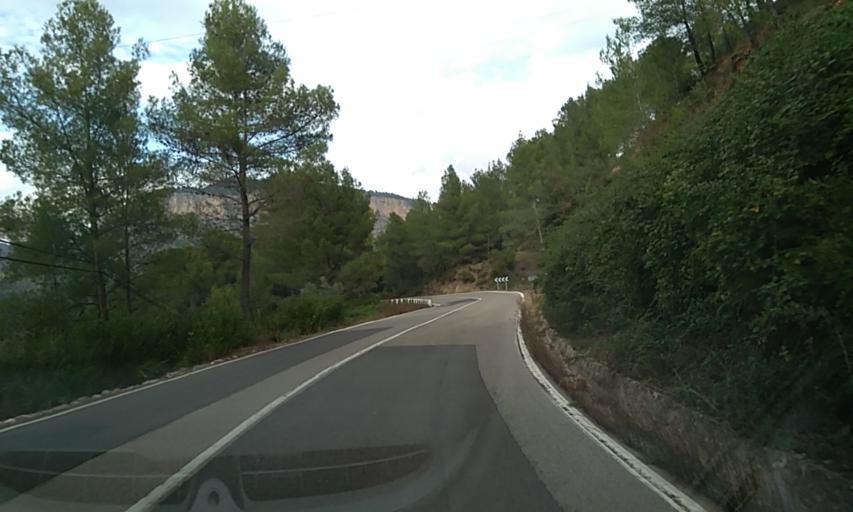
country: ES
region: Valencia
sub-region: Provincia de Castello
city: Puebla de Arenoso
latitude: 40.0871
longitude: -0.5629
